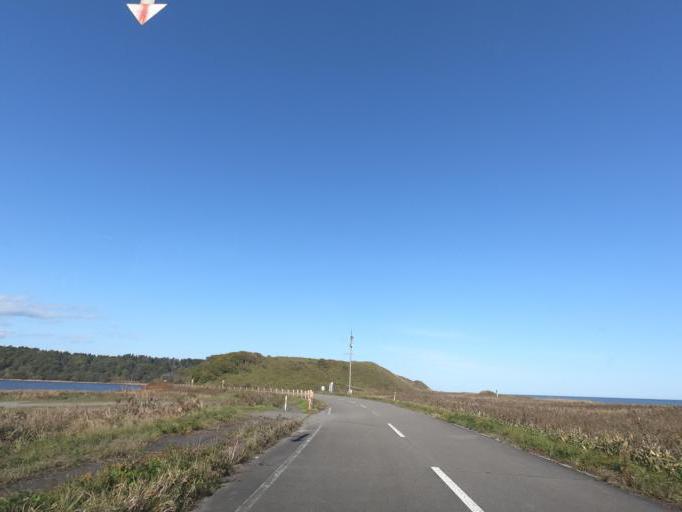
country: JP
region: Hokkaido
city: Obihiro
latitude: 42.5996
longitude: 143.5492
